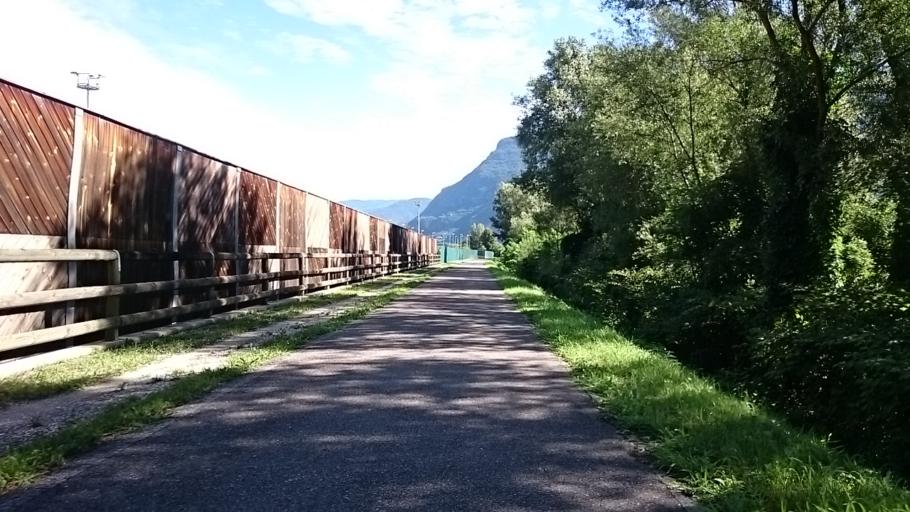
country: IT
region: Trentino-Alto Adige
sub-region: Bolzano
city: Vadena
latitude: 46.4318
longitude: 11.3124
